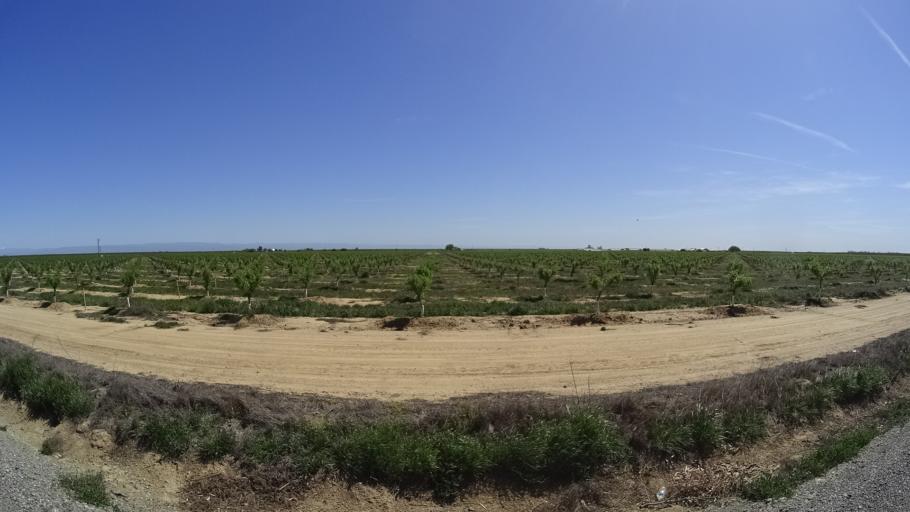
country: US
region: California
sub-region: Glenn County
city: Orland
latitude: 39.6470
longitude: -122.1409
